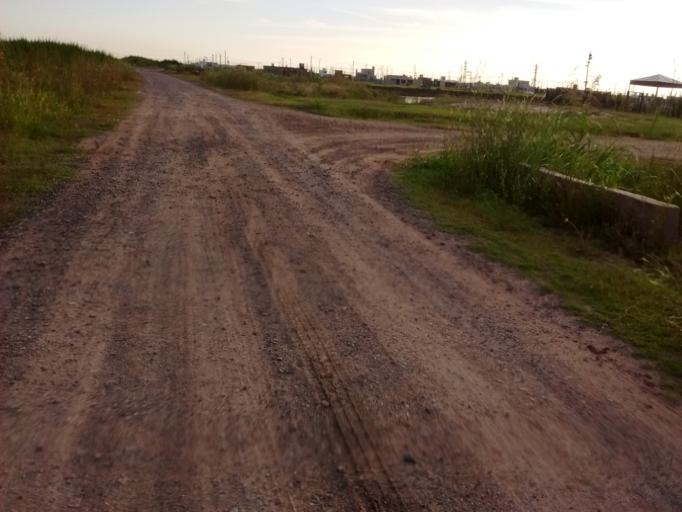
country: AR
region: Santa Fe
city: Roldan
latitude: -32.9406
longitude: -60.8749
